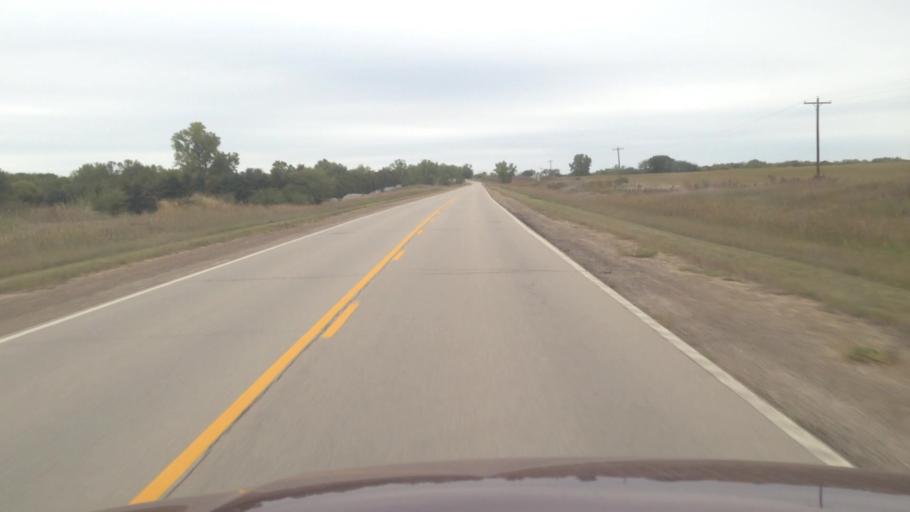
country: US
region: Kansas
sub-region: Jefferson County
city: Oskaloosa
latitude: 39.1184
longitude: -95.4837
